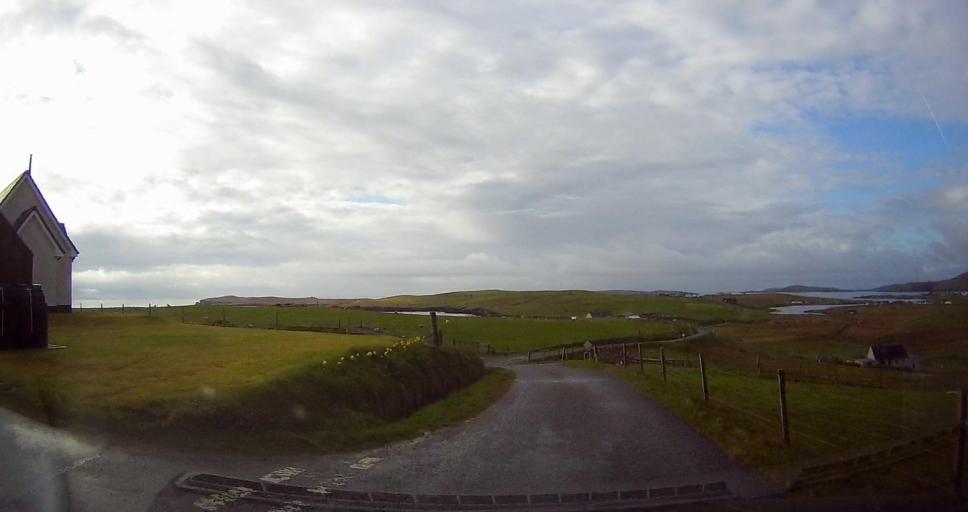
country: GB
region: Scotland
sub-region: Shetland Islands
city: Sandwick
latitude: 60.0541
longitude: -1.2082
